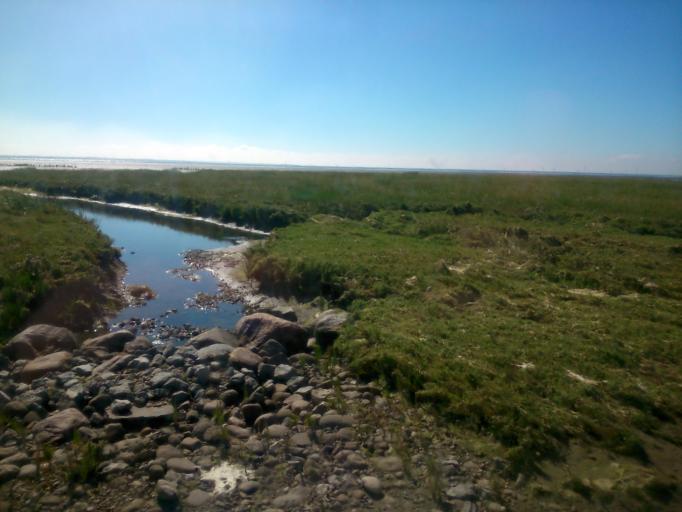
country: DK
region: South Denmark
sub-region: Esbjerg Kommune
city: Ribe
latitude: 55.3028
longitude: 8.6207
